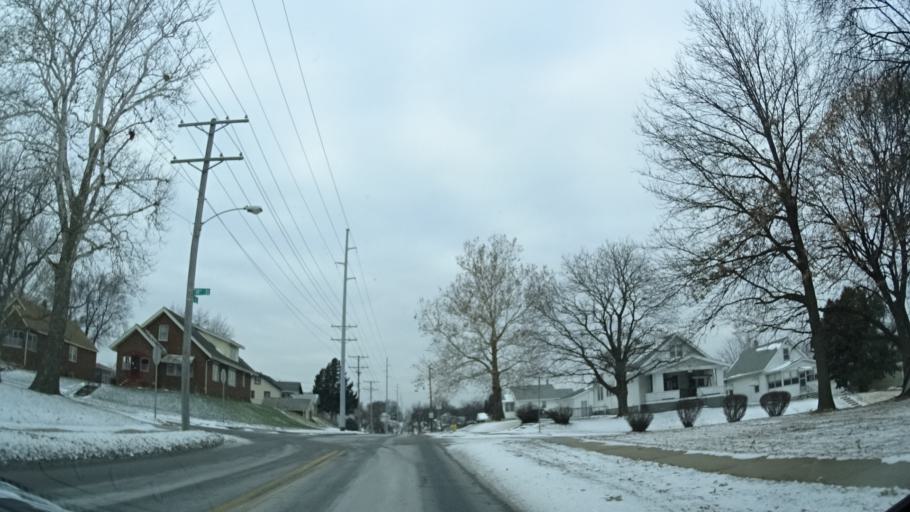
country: US
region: Nebraska
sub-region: Douglas County
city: Omaha
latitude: 41.2198
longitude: -95.9696
